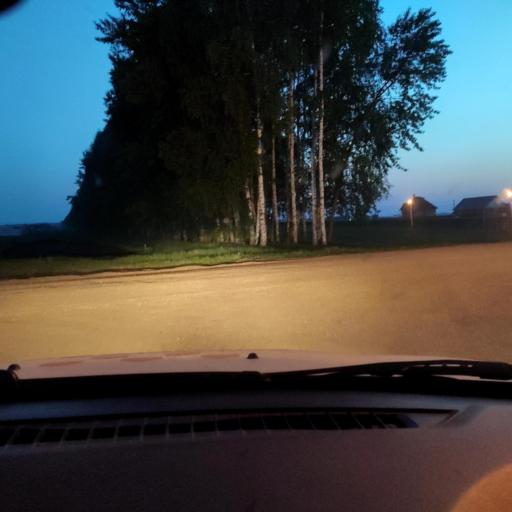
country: RU
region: Bashkortostan
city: Karmaskaly
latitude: 54.3539
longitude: 56.1439
